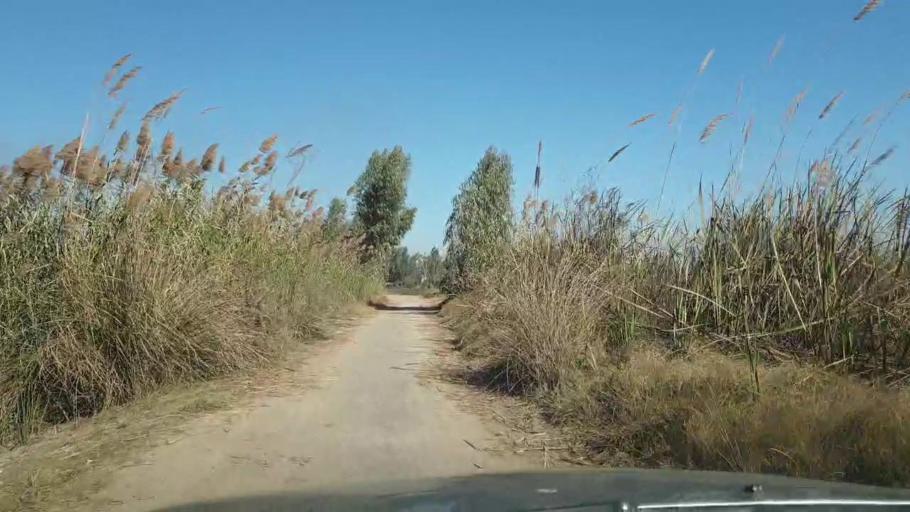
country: PK
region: Sindh
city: Ghotki
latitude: 28.0314
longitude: 69.2884
